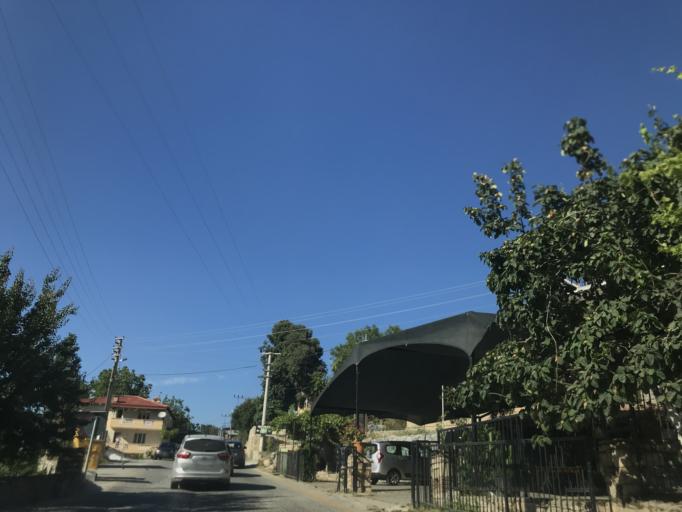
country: TR
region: Aydin
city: Davutlar
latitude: 37.7365
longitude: 27.3401
